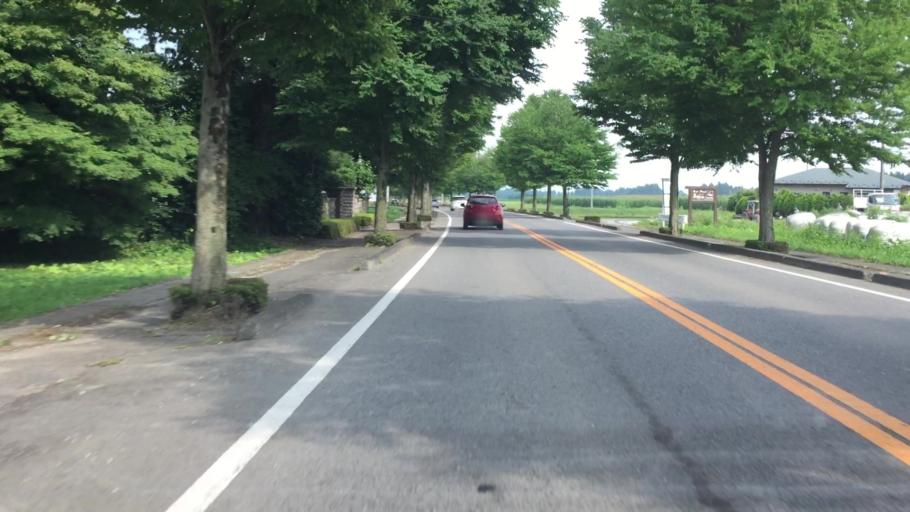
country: JP
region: Tochigi
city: Kuroiso
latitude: 36.9916
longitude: 139.9426
